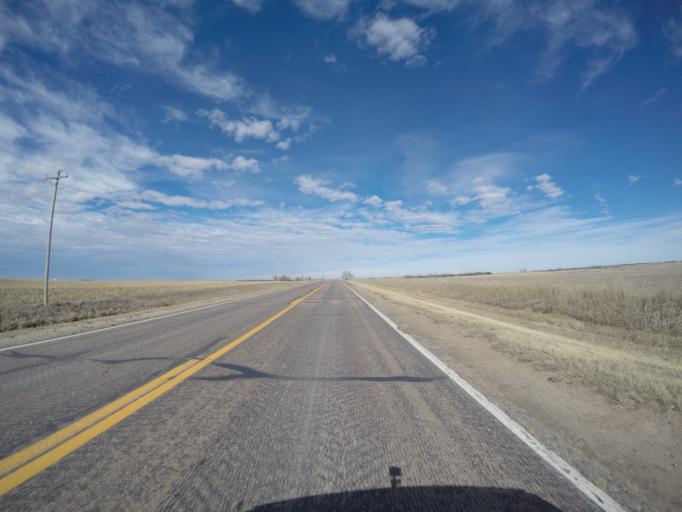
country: US
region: Nebraska
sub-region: Franklin County
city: Franklin
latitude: 40.2877
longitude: -98.9525
